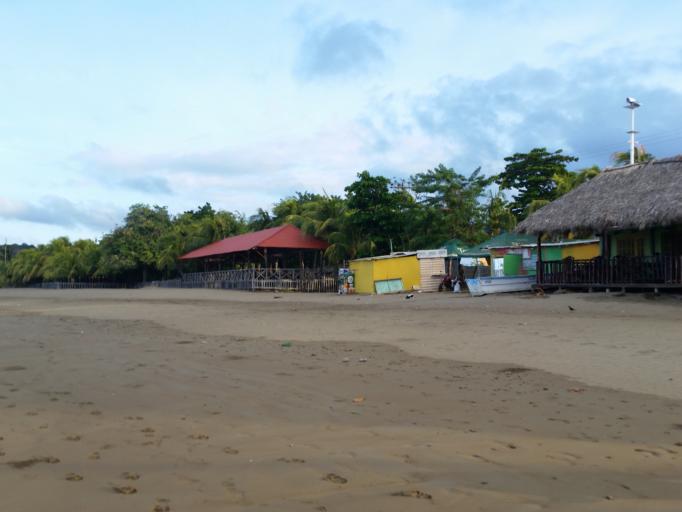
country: NI
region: Rivas
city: San Juan del Sur
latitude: 11.2565
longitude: -85.8732
